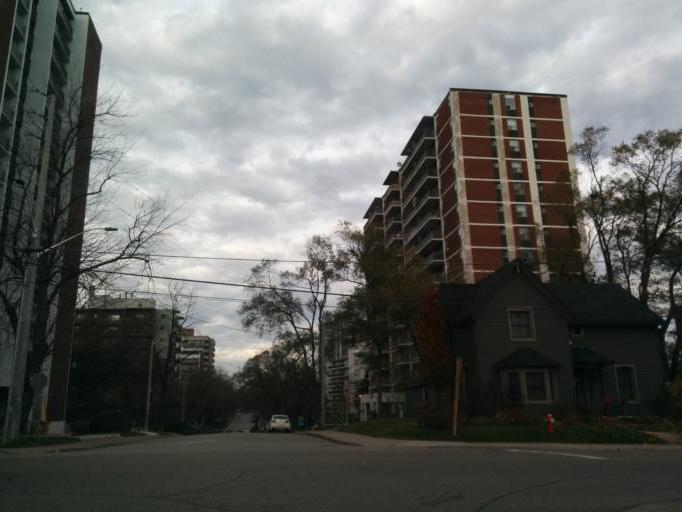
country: CA
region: Ontario
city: Mississauga
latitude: 43.5528
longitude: -79.5864
